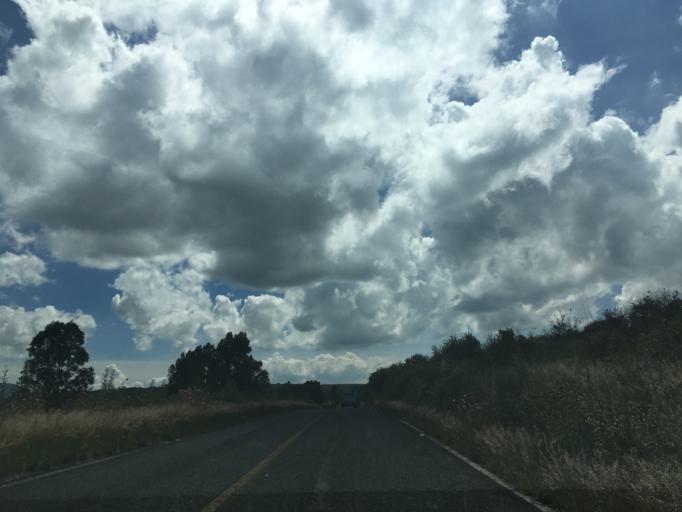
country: MX
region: Michoacan
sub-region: Morelia
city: Cuto de la Esperanza
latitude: 19.7798
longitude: -101.4013
